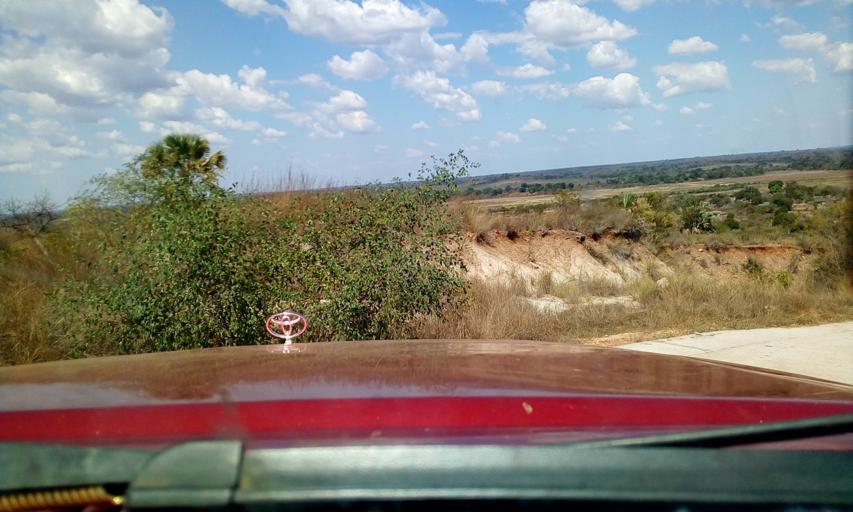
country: MG
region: Boeny
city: Sitampiky
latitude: -16.1204
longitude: 45.4721
